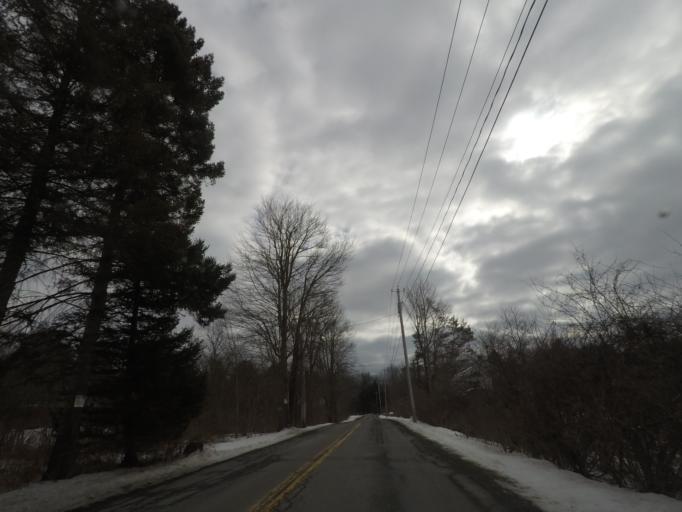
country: US
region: New York
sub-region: Rensselaer County
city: Hoosick Falls
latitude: 42.9441
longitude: -73.4332
